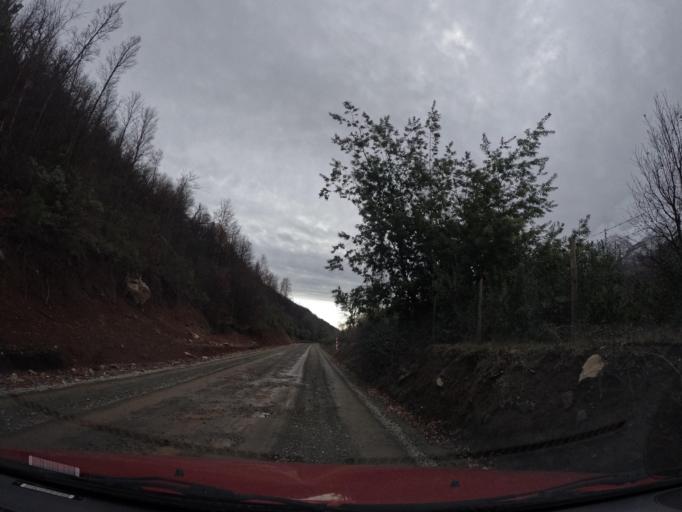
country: CL
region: Maule
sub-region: Provincia de Linares
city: Colbun
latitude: -35.8582
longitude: -71.1463
